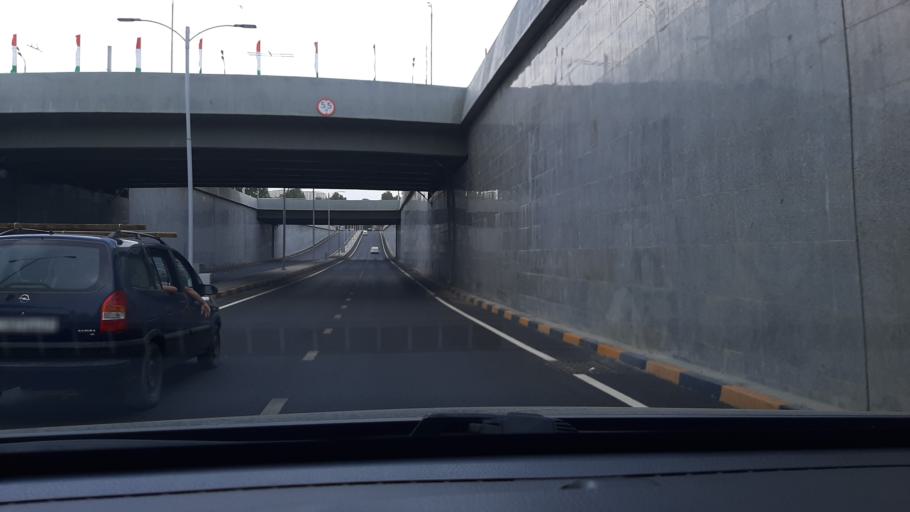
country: TJ
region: Dushanbe
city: Dushanbe
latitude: 38.5837
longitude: 68.7553
